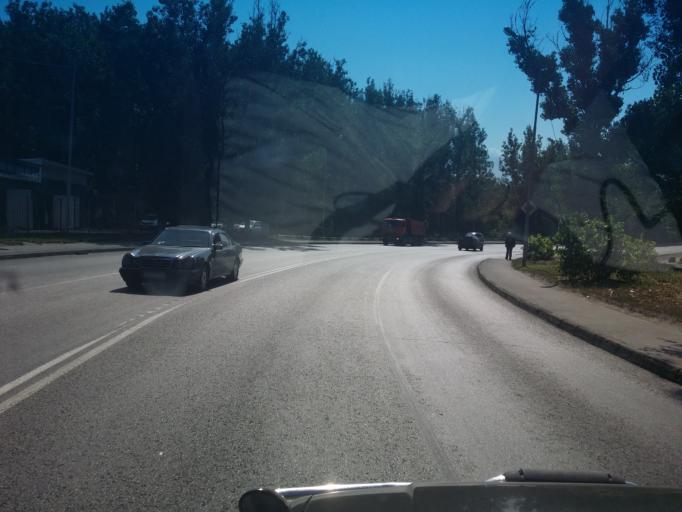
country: KZ
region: Almaty Oblysy
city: Pervomayskiy
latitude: 43.3504
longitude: 76.9626
